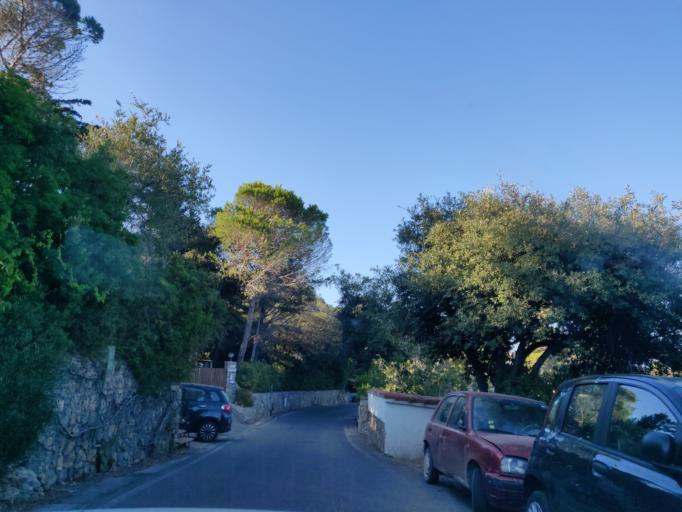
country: IT
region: Tuscany
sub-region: Provincia di Grosseto
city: Orbetello Scalo
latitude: 42.4110
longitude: 11.2923
